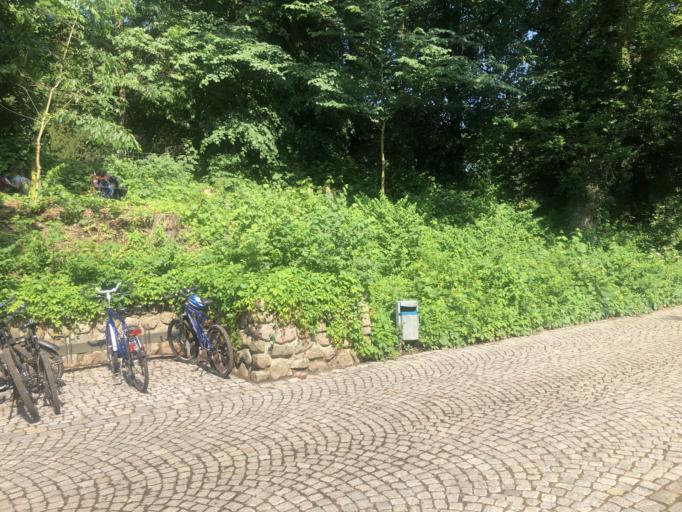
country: DE
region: Schleswig-Holstein
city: Busdorf
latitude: 54.4975
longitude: 9.5693
